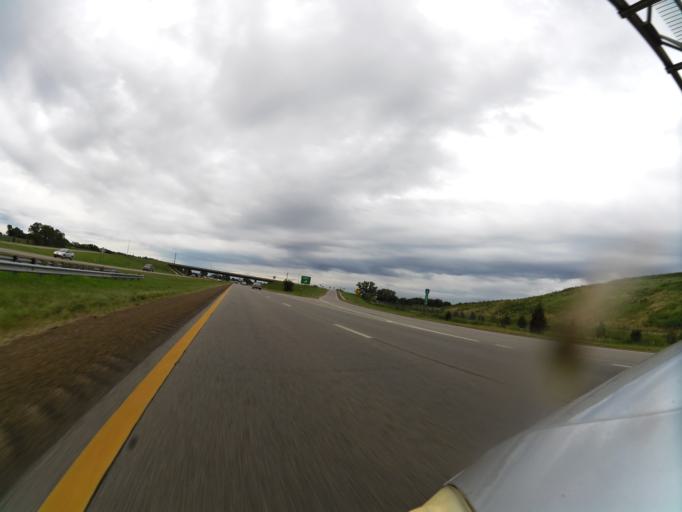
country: US
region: Kansas
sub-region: Sedgwick County
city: Maize
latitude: 37.7573
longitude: -97.3929
